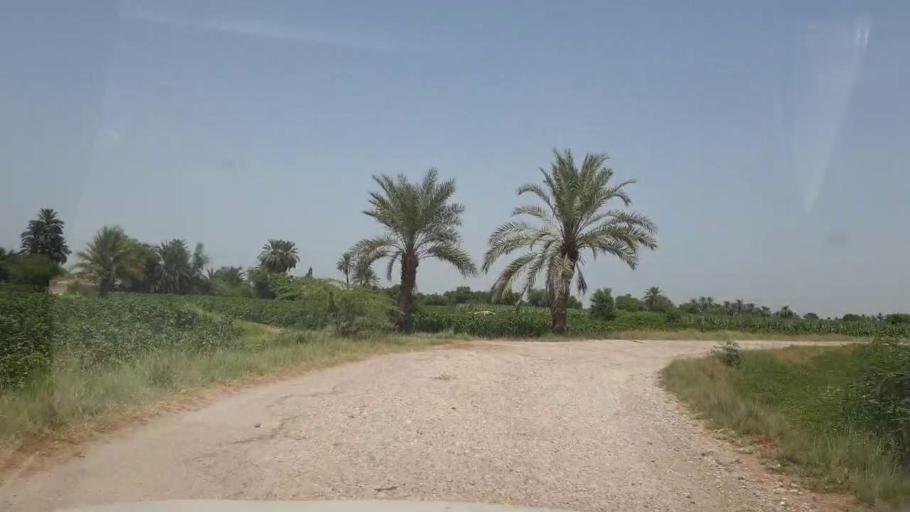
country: PK
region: Sindh
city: Bozdar
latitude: 27.1715
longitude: 68.6258
